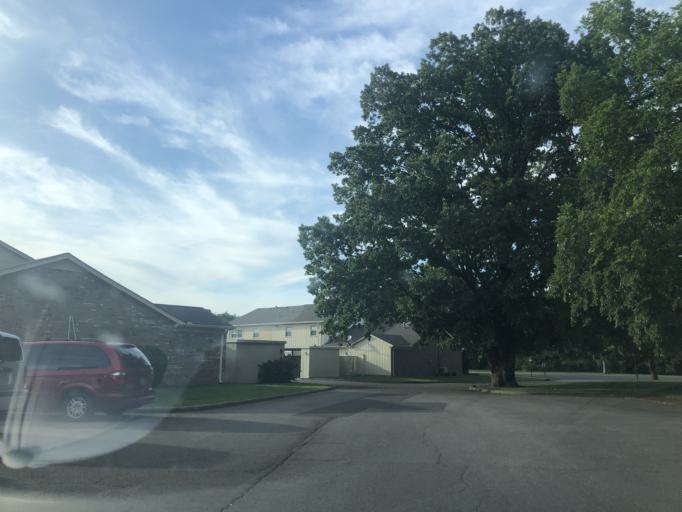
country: US
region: Tennessee
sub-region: Davidson County
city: Belle Meade
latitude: 36.0699
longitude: -86.9463
